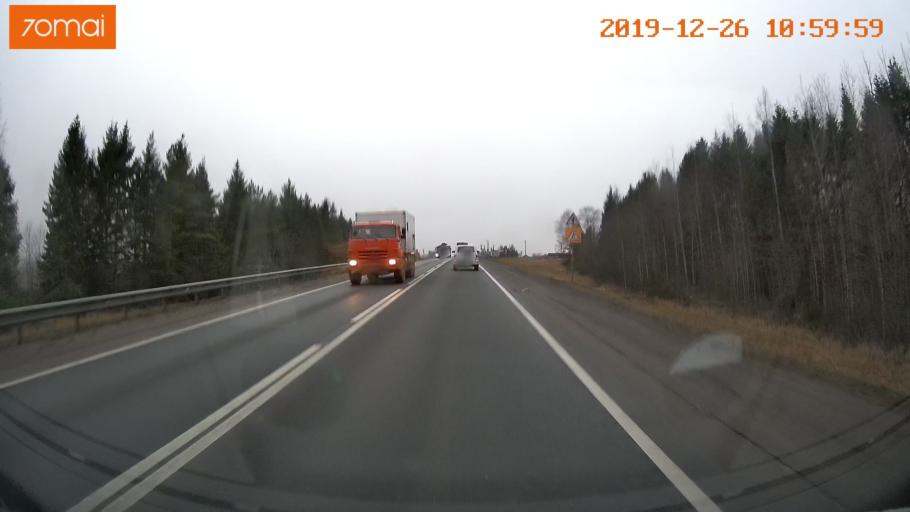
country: RU
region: Vologda
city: Molochnoye
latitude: 59.1684
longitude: 39.4590
